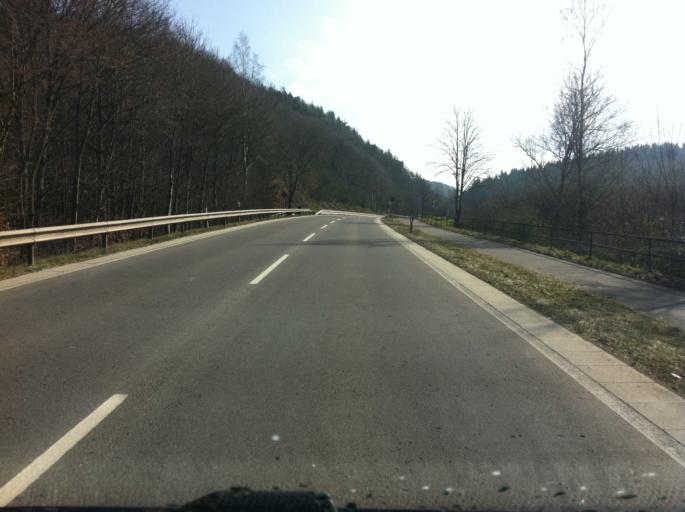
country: DE
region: North Rhine-Westphalia
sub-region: Regierungsbezirk Koln
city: Bad Munstereifel
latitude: 50.5279
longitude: 6.7820
